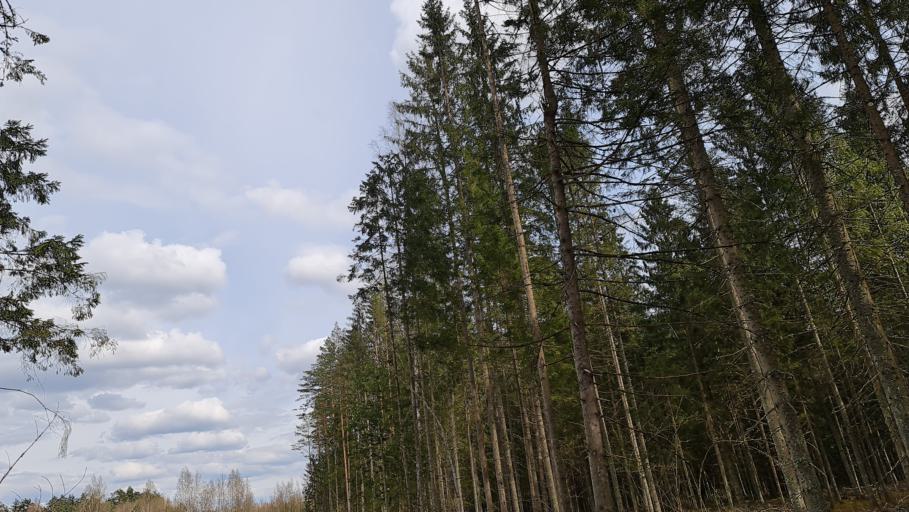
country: BY
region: Vitebsk
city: Byahoml'
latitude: 54.7495
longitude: 28.0460
